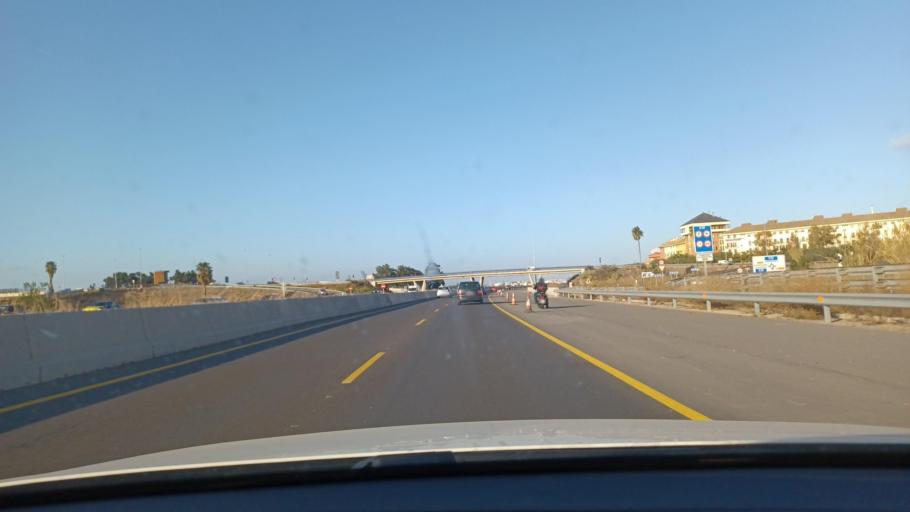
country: ES
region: Valencia
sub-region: Provincia de Valencia
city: Alboraya
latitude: 39.5066
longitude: -0.3257
